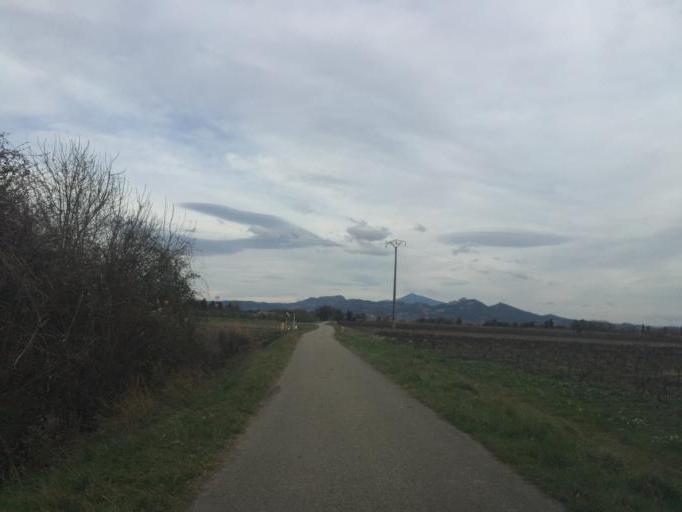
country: FR
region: Provence-Alpes-Cote d'Azur
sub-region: Departement du Vaucluse
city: Camaret-sur-Aigues
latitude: 44.1570
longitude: 4.8980
